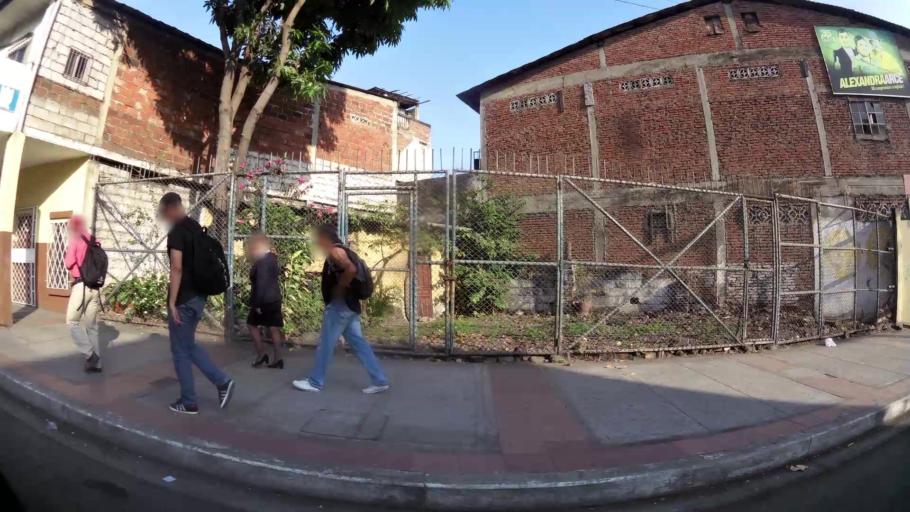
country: EC
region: Guayas
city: Eloy Alfaro
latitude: -2.1768
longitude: -79.8537
